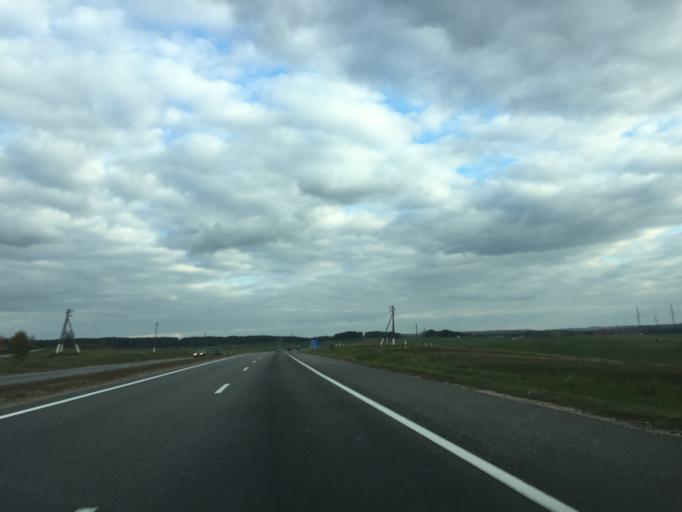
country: BY
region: Minsk
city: Rakaw
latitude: 53.9778
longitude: 27.0541
